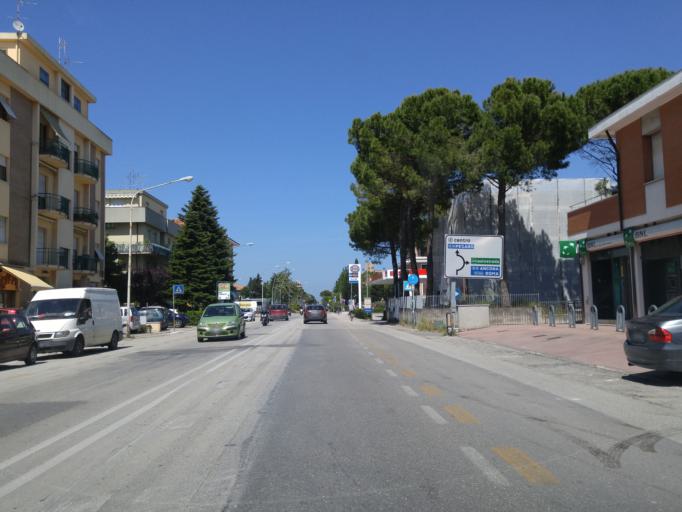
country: IT
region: The Marches
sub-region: Provincia di Pesaro e Urbino
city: Fano
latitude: 43.8354
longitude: 13.0052
